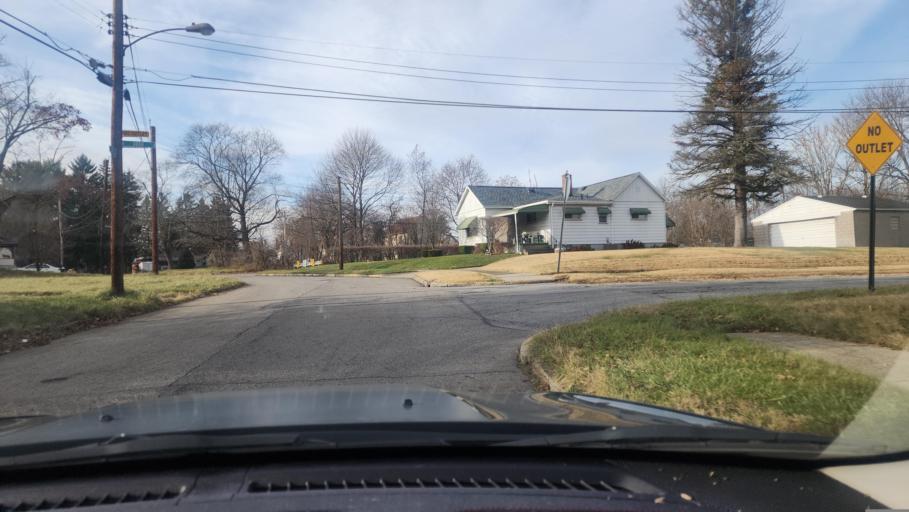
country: US
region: Ohio
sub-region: Mahoning County
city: Youngstown
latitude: 41.0996
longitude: -80.6233
